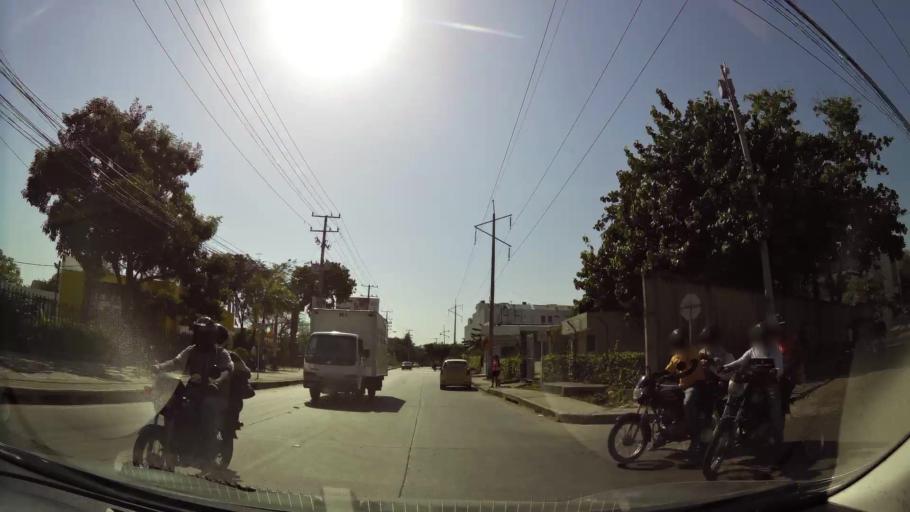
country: CO
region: Bolivar
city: Cartagena
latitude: 10.3895
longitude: -75.4686
